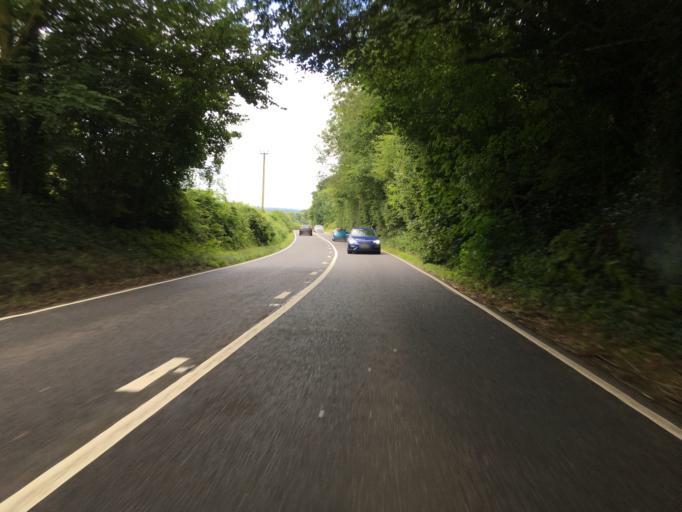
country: GB
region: England
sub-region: Hampshire
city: Petersfield
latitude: 51.0095
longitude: -0.9862
